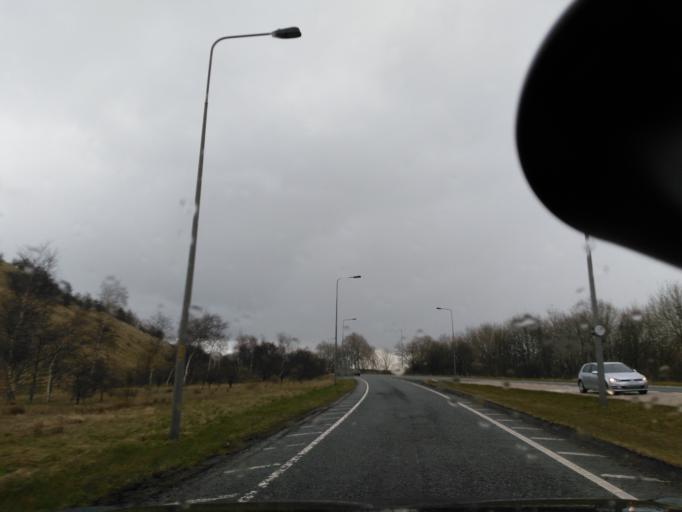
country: GB
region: England
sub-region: North Yorkshire
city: Embsay
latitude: 53.9686
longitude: -1.9962
